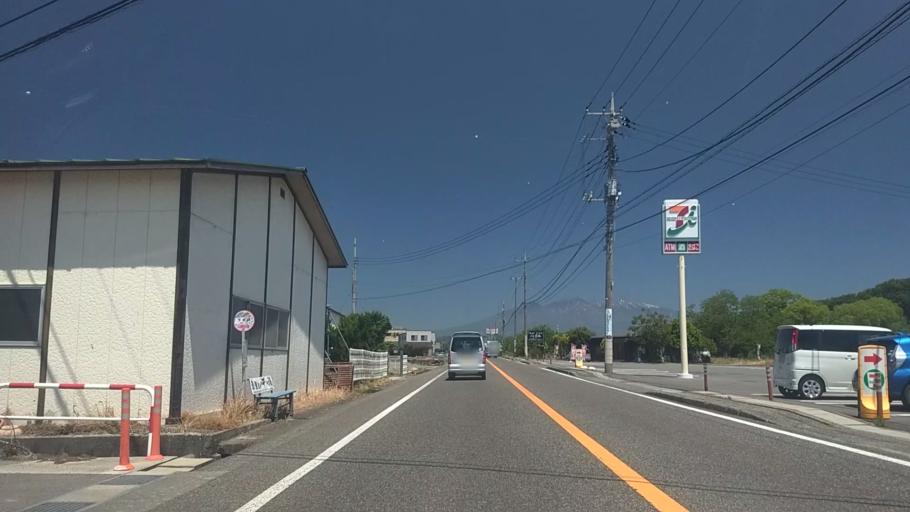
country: JP
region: Yamanashi
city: Nirasaki
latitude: 35.7417
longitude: 138.4427
